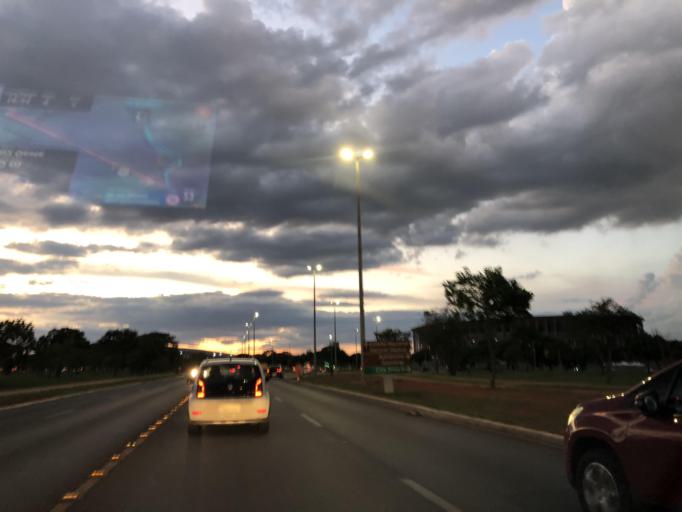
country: BR
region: Federal District
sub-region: Brasilia
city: Brasilia
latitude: -15.7879
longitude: -47.8930
